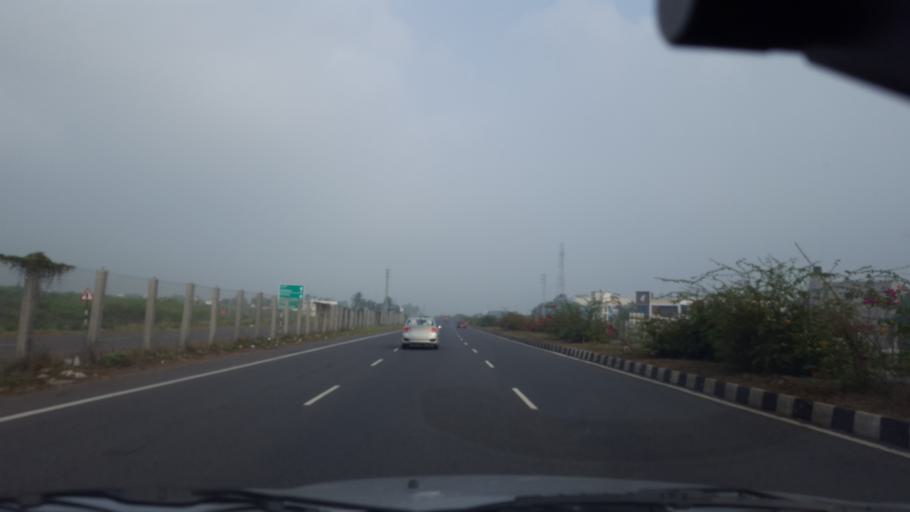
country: IN
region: Andhra Pradesh
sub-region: Prakasam
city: Ongole
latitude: 15.5570
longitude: 80.0535
